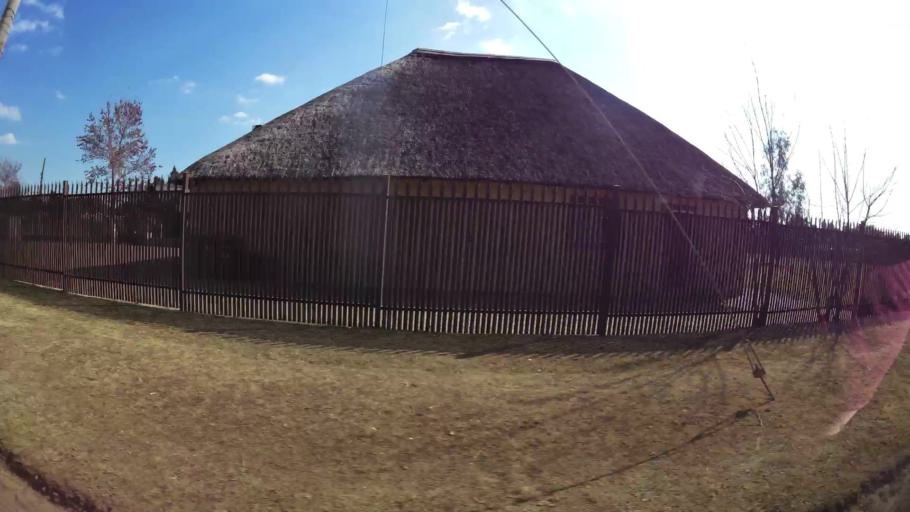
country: ZA
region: Gauteng
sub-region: Ekurhuleni Metropolitan Municipality
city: Benoni
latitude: -26.0962
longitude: 28.3497
